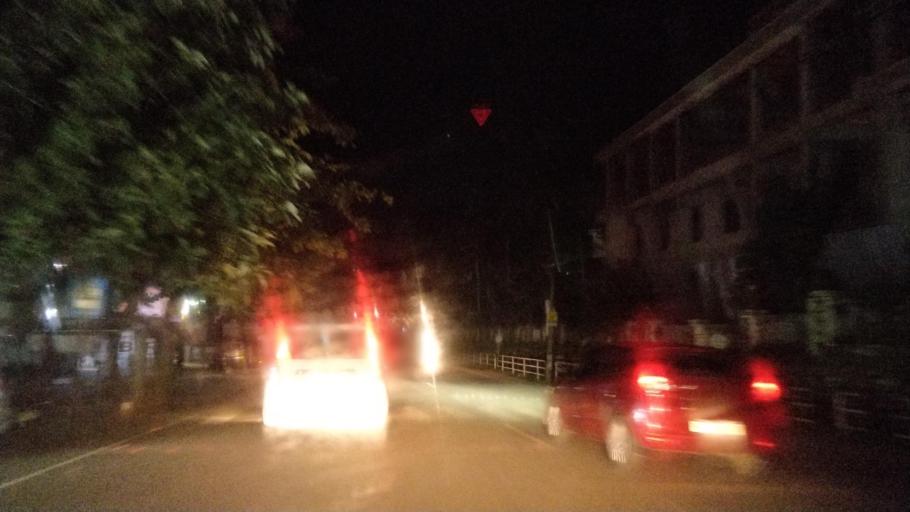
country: IN
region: Kerala
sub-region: Kottayam
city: Kottayam
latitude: 9.6334
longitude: 76.5237
